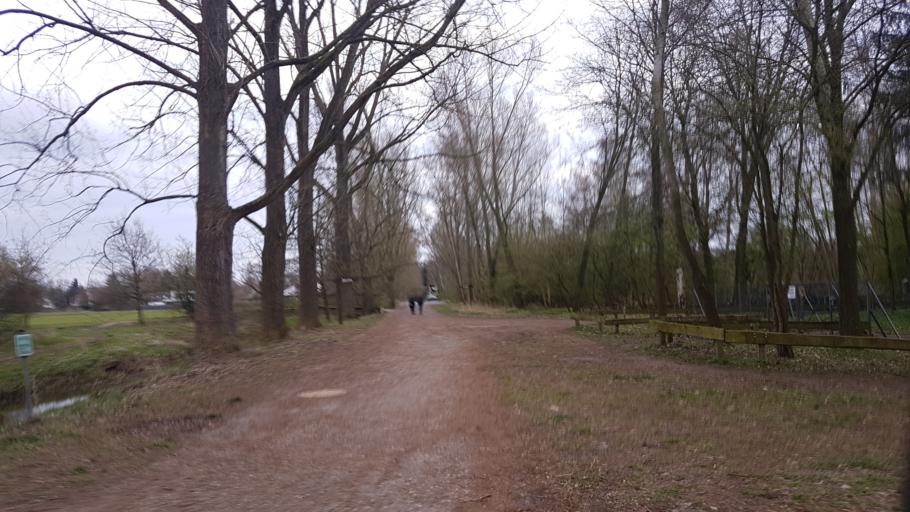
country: DE
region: Lower Saxony
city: Langenhagen
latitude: 52.4395
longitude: 9.7891
